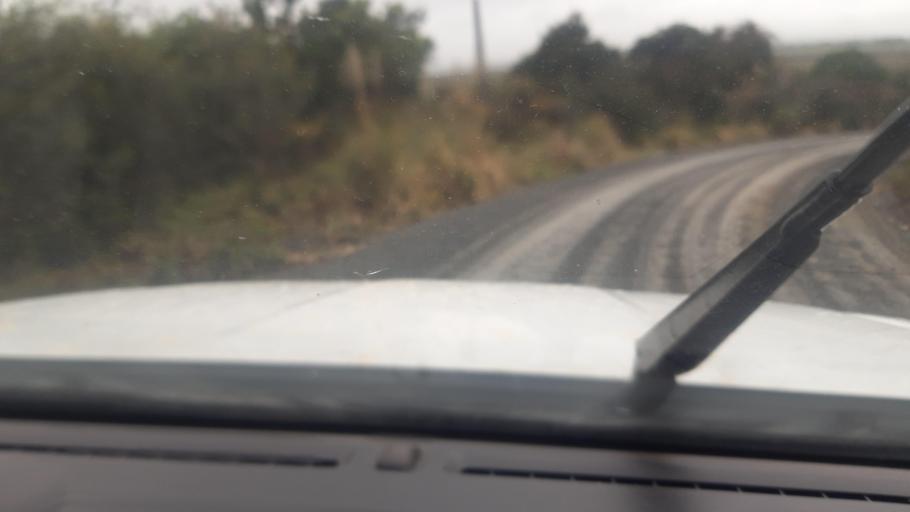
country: NZ
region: Northland
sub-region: Far North District
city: Kaitaia
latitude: -34.9911
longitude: 173.2145
